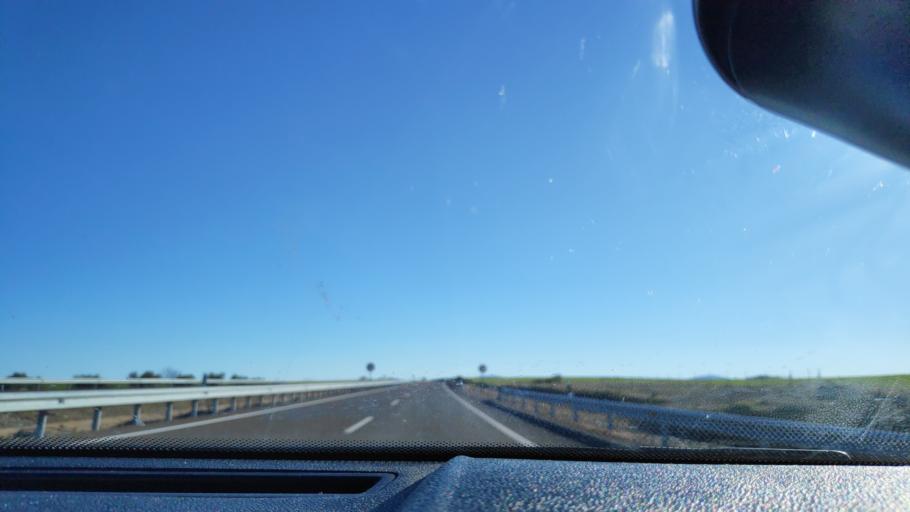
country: ES
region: Extremadura
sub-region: Provincia de Badajoz
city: Fuente de Cantos
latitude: 38.2079
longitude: -6.2867
